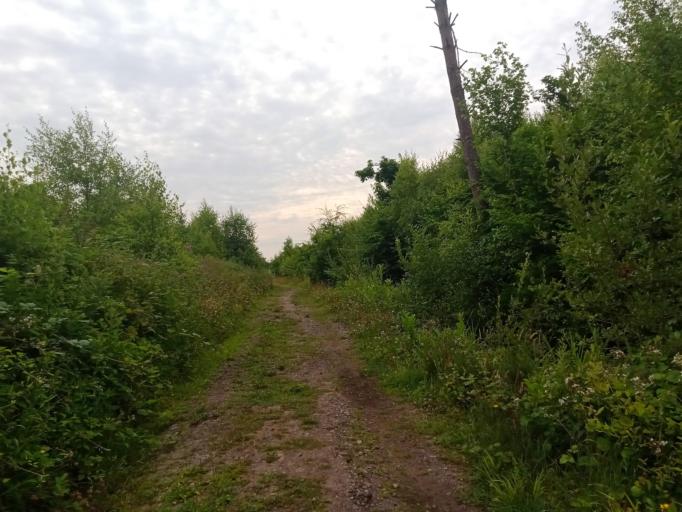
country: IE
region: Leinster
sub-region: Laois
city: Abbeyleix
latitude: 52.9073
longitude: -7.3605
